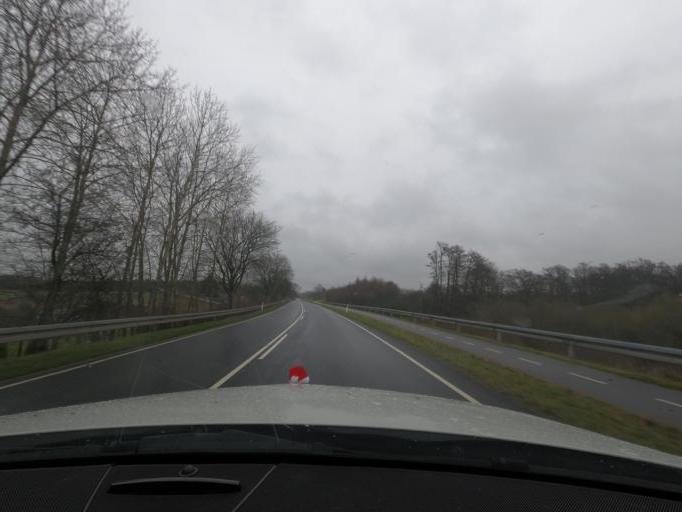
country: DK
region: South Denmark
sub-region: Haderslev Kommune
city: Starup
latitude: 55.2435
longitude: 9.5567
